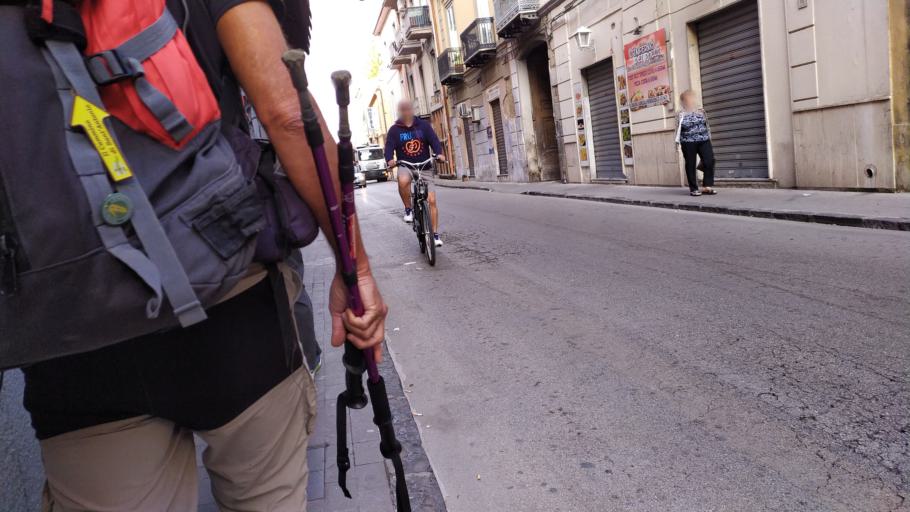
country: IT
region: Campania
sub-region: Provincia di Caserta
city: San Nicola la Strada
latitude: 41.0688
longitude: 14.3320
